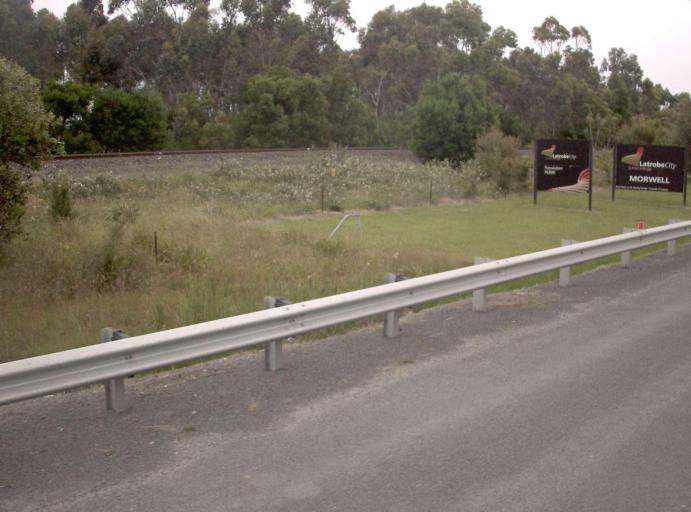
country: AU
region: Victoria
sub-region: Latrobe
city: Morwell
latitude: -38.2244
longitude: 146.4666
